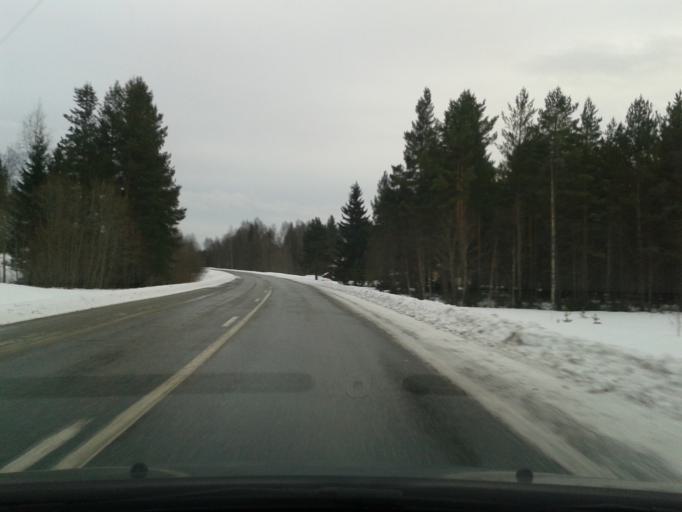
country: SE
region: Vaesternorrland
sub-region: Solleftea Kommun
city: As
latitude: 63.5996
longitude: 16.8175
